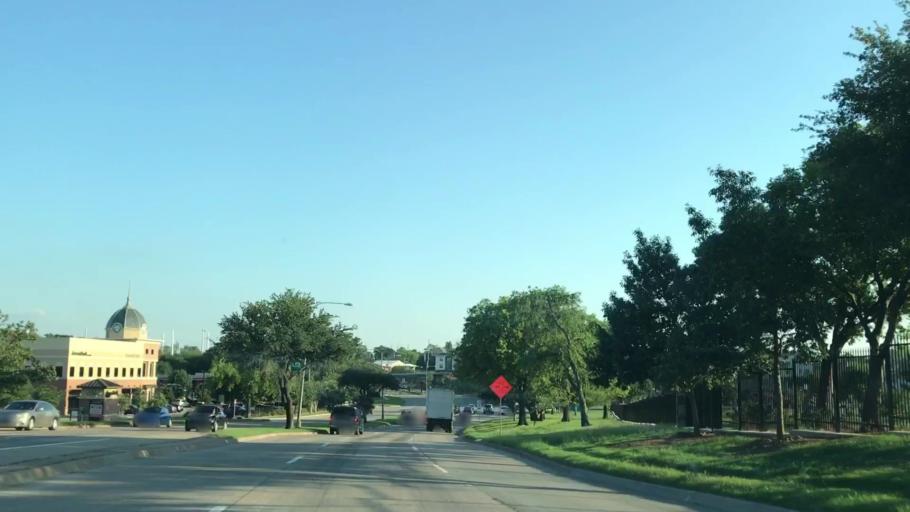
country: US
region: Texas
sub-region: Denton County
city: Denton
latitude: 33.2082
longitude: -97.1370
